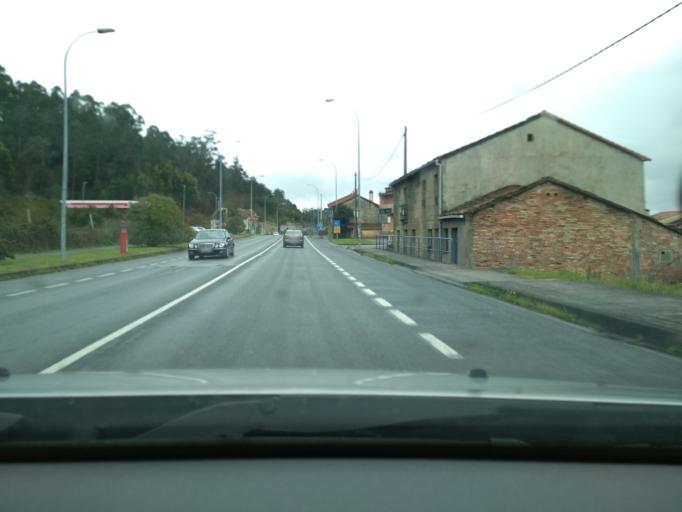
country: ES
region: Galicia
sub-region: Provincia da Coruna
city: Padron
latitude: 42.7620
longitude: -8.6516
